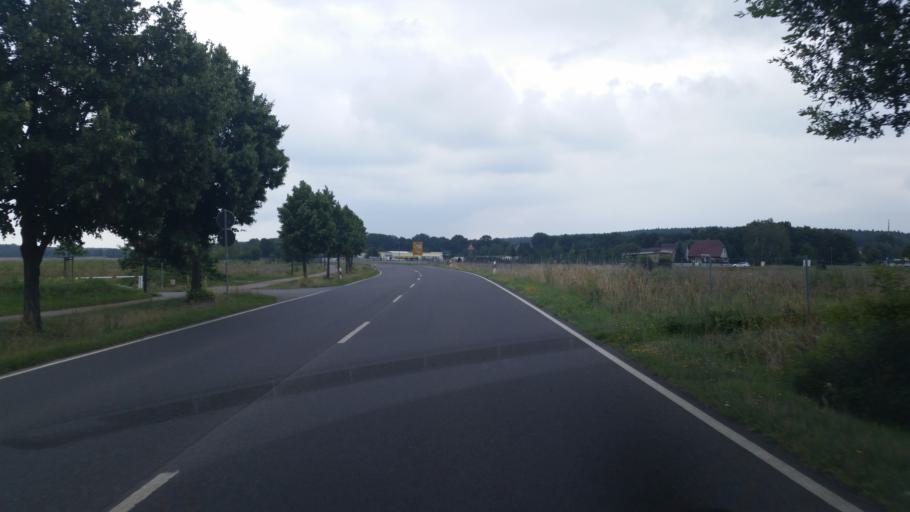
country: DE
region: Brandenburg
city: Senftenberg
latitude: 51.5012
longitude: 14.0638
